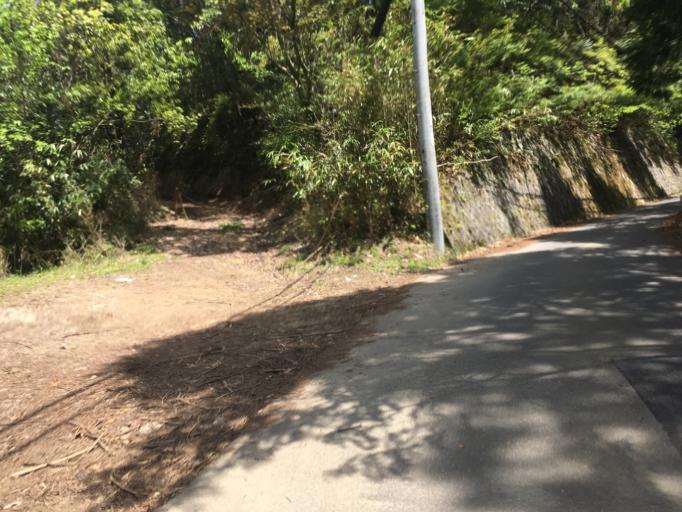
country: JP
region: Kyoto
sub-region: Kyoto-shi
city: Kamigyo-ku
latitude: 35.0766
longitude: 135.7185
